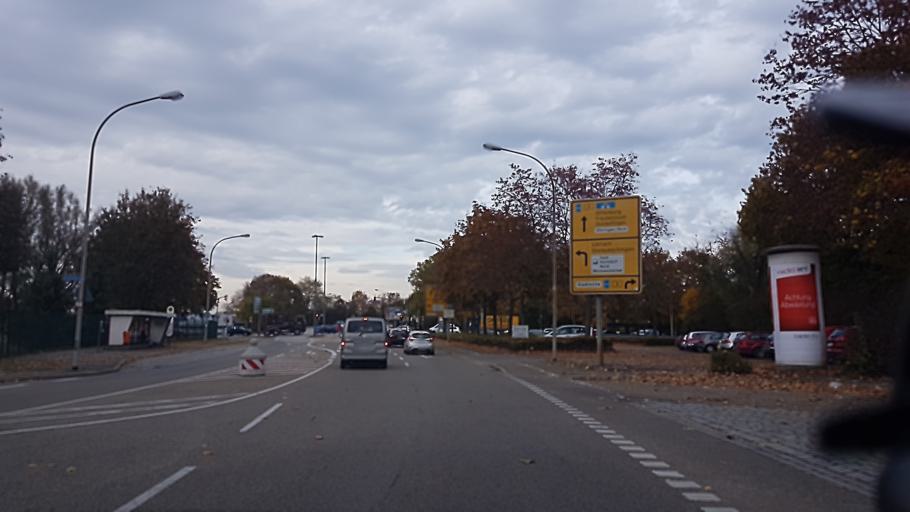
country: DE
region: Baden-Wuerttemberg
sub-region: Freiburg Region
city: Gundelfingen
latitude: 48.0325
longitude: 7.8604
